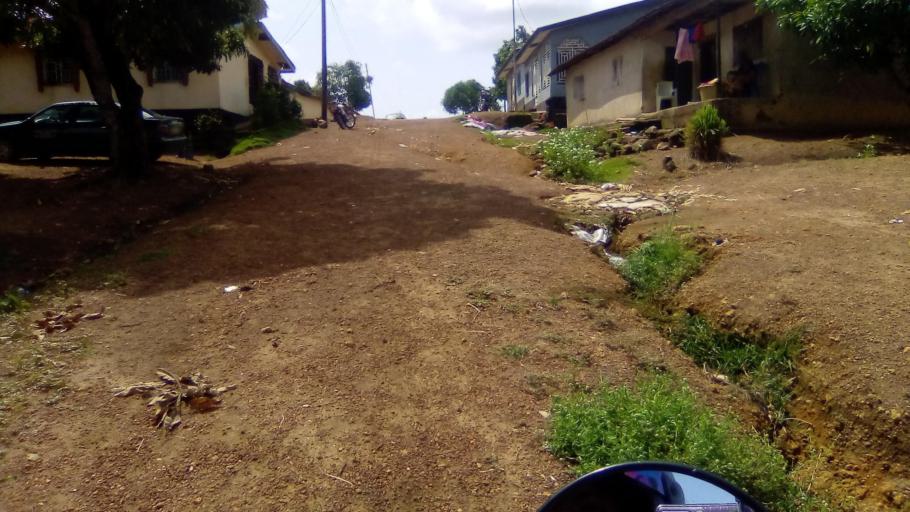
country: SL
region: Southern Province
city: Bo
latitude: 7.9798
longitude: -11.7460
